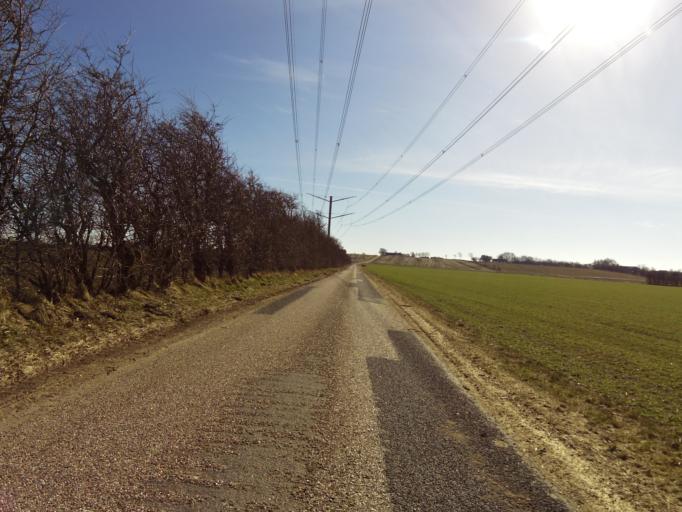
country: DK
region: South Denmark
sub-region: Tonder Kommune
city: Toftlund
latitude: 55.2181
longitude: 9.1487
